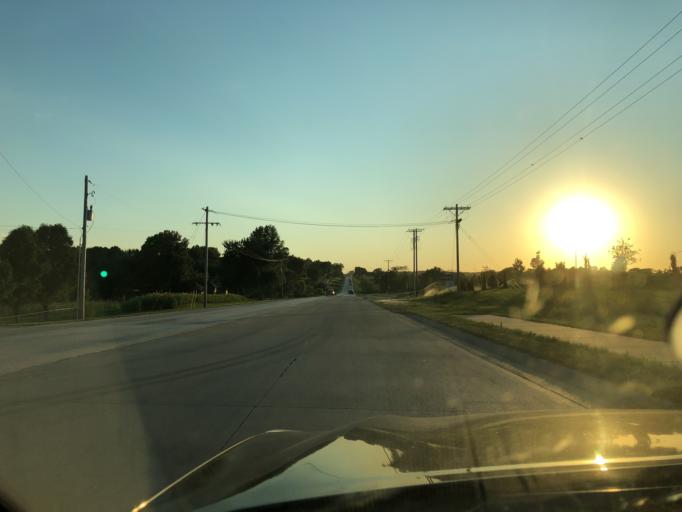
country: US
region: Kansas
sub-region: Leavenworth County
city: Lansing
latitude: 39.2667
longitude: -94.9371
